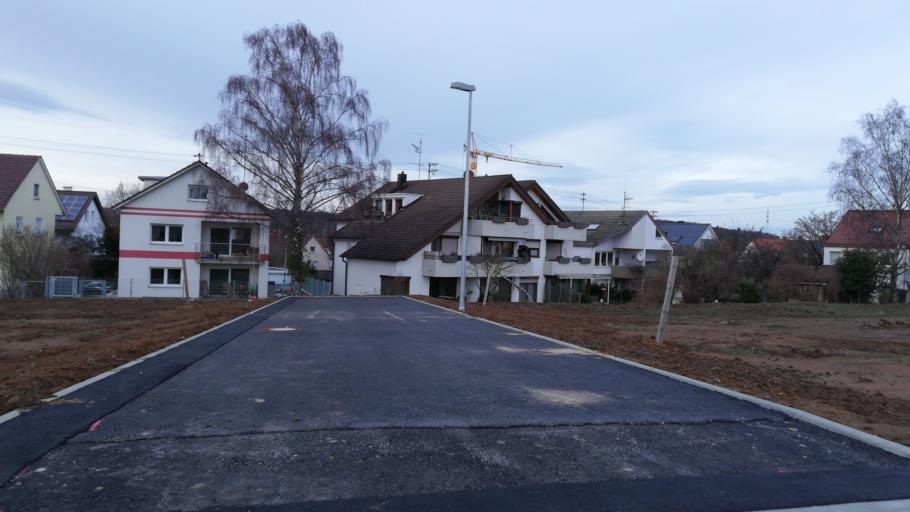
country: DE
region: Baden-Wuerttemberg
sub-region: Regierungsbezirk Stuttgart
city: Schwaikheim
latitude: 48.8887
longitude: 9.3193
